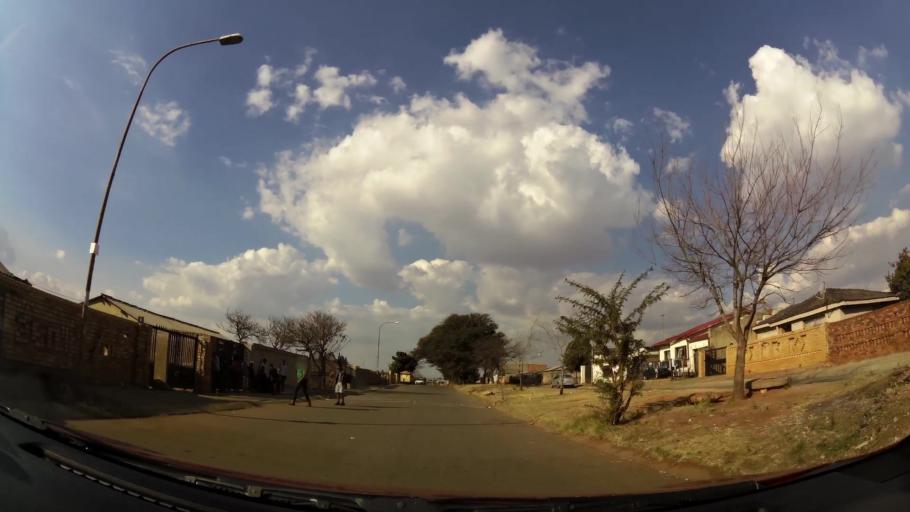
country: ZA
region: Gauteng
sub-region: City of Johannesburg Metropolitan Municipality
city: Soweto
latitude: -26.2287
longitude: 27.8706
